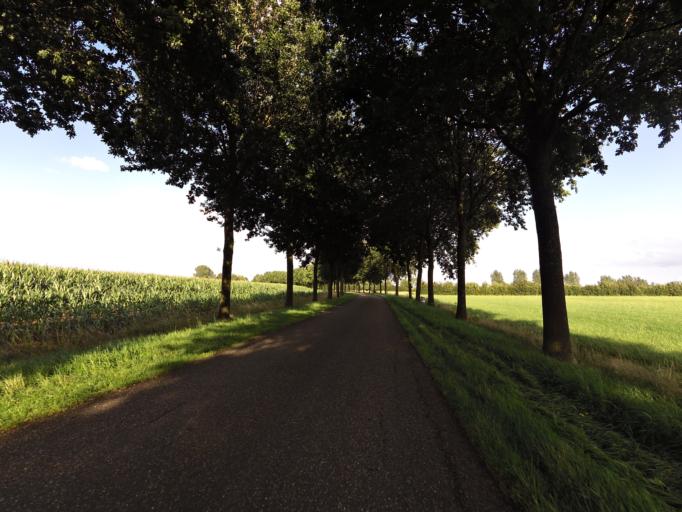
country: NL
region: Gelderland
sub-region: Gemeente Doesburg
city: Doesburg
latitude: 51.9802
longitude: 6.1081
